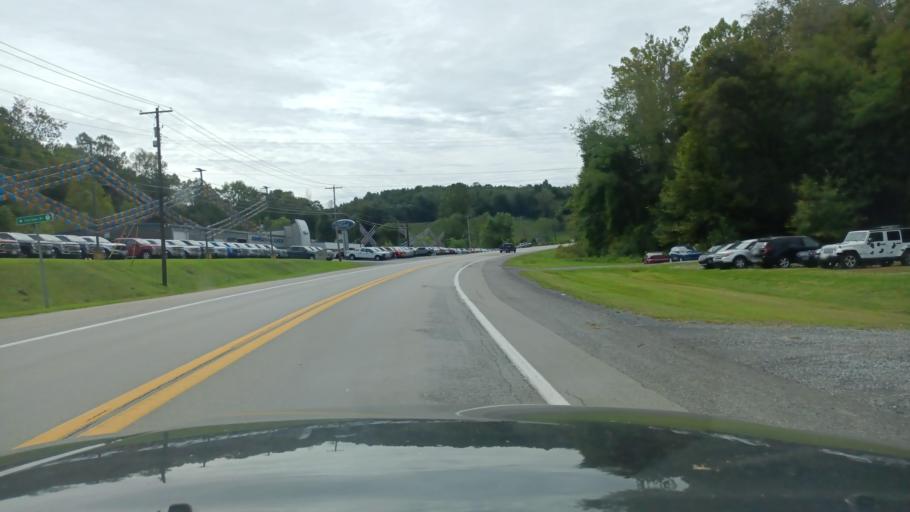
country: US
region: West Virginia
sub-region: Taylor County
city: Grafton
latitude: 39.3393
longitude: -80.0610
